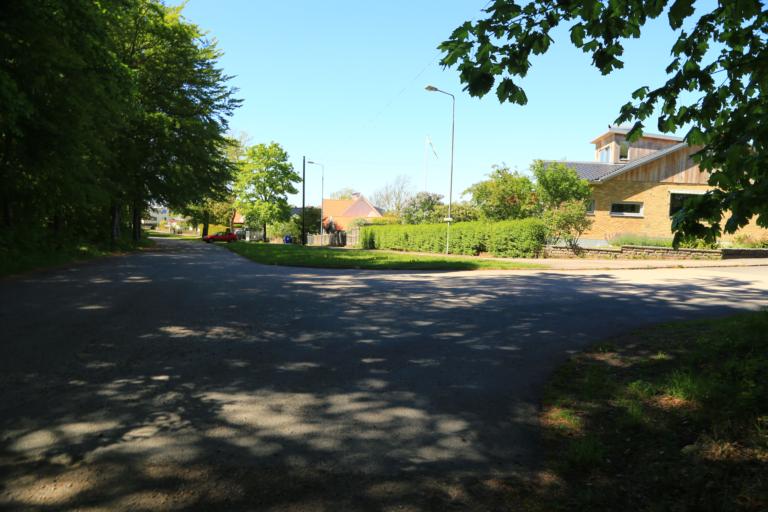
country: SE
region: Halland
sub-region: Varbergs Kommun
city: Varberg
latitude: 57.0991
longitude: 12.2711
